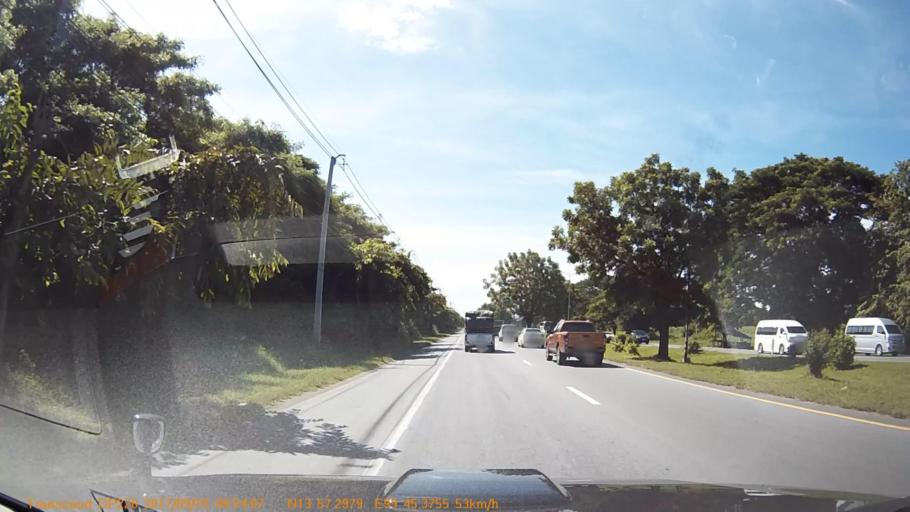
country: TH
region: Kanchanaburi
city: Tha Maka
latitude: 13.9548
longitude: 99.7563
